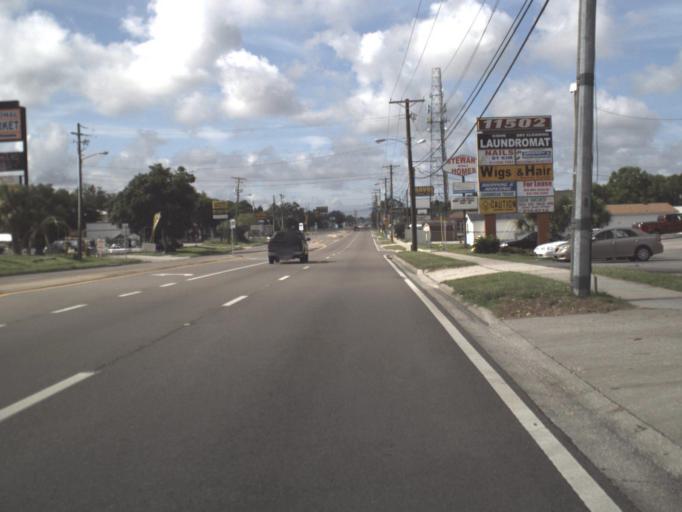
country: US
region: Florida
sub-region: Hillsborough County
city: University
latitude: 28.0529
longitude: -82.4513
